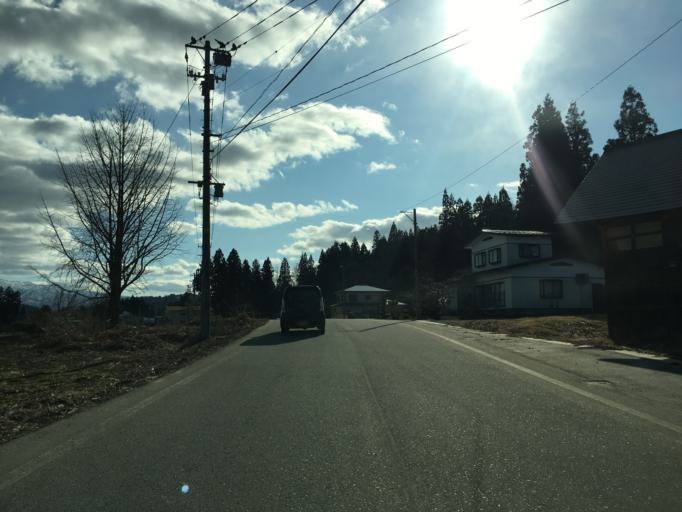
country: JP
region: Yamagata
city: Yonezawa
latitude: 37.9660
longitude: 139.9916
